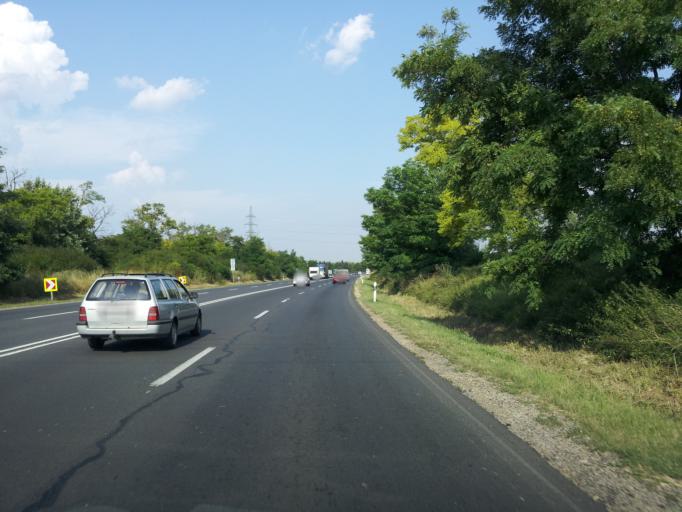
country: HU
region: Veszprem
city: Veszprem
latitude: 47.1011
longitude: 17.9388
